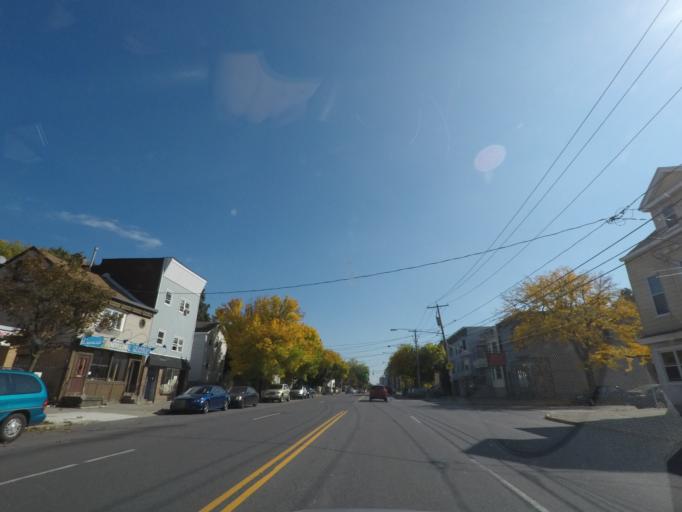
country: US
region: New York
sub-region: Albany County
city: Albany
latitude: 42.6628
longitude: -73.7739
